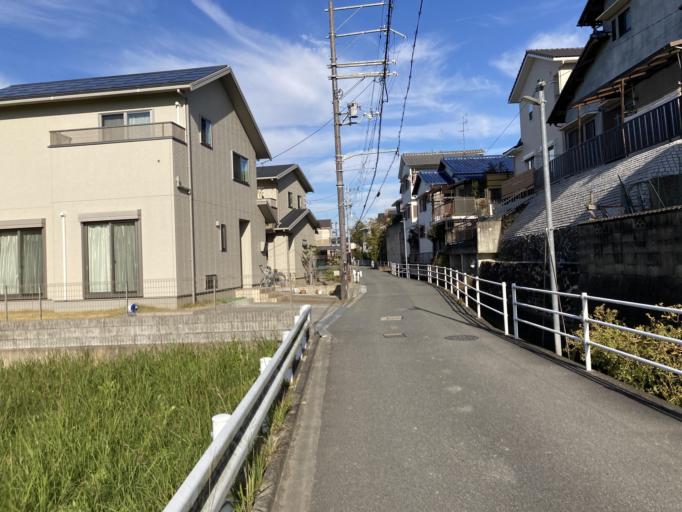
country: JP
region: Nara
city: Nara-shi
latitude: 34.6700
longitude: 135.7766
